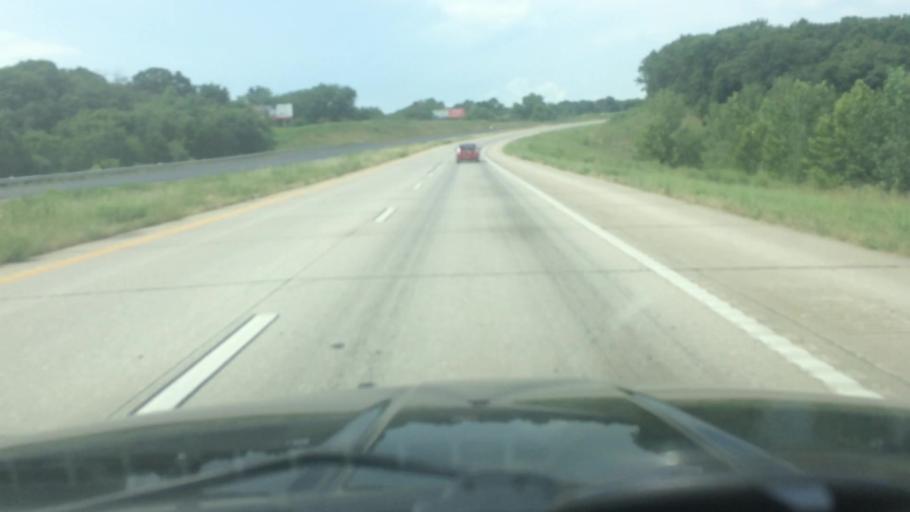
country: US
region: Missouri
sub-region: Saint Clair County
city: Osceola
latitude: 38.0843
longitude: -93.7063
